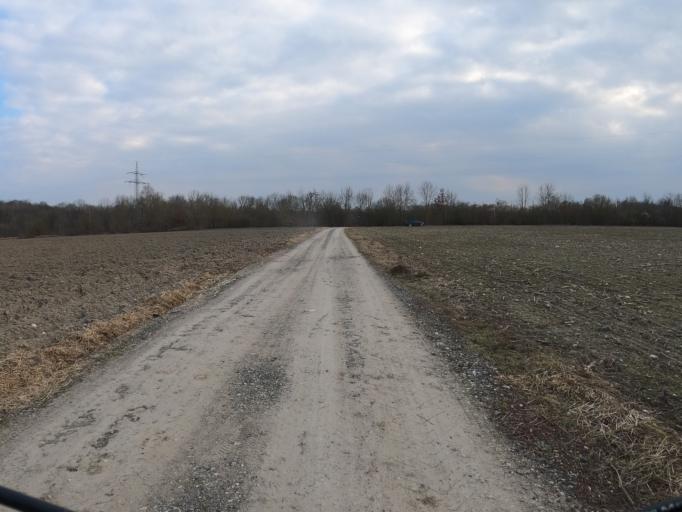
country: DE
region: Bavaria
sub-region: Swabia
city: Nersingen
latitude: 48.4482
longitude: 10.1079
